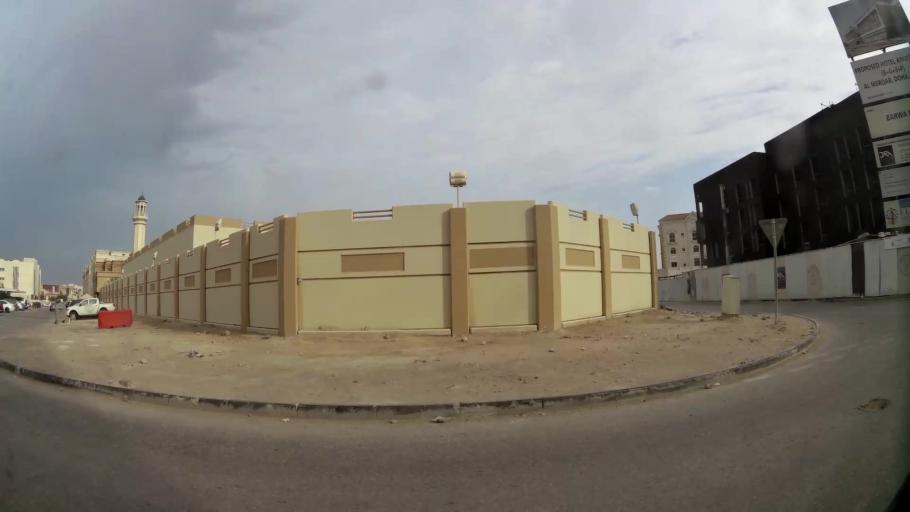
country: QA
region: Baladiyat ad Dawhah
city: Doha
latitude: 25.2779
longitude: 51.4937
